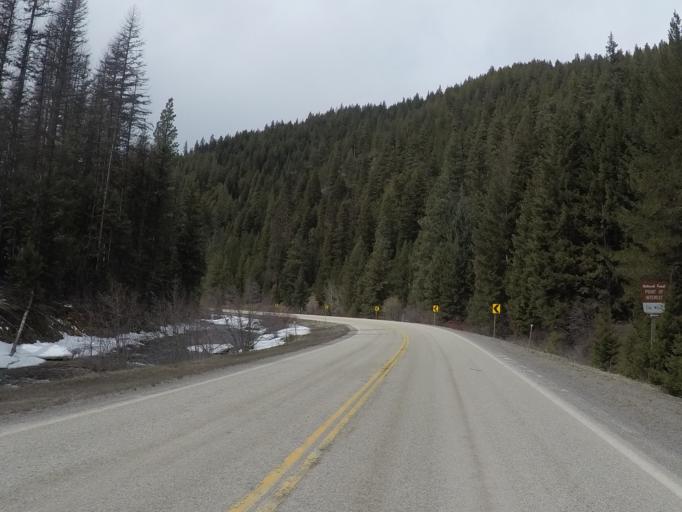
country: US
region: Montana
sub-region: Missoula County
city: Frenchtown
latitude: 46.7693
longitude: -114.4611
